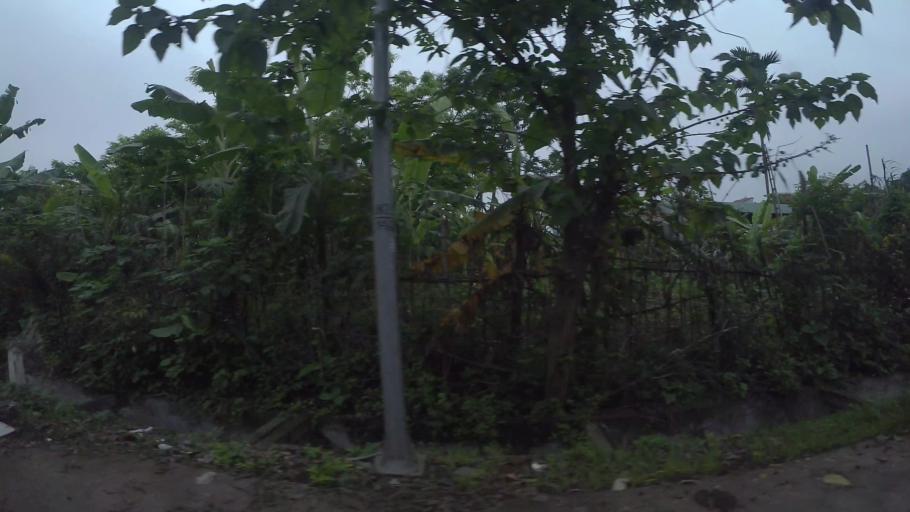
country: VN
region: Hung Yen
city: Van Giang
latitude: 20.9744
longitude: 105.8915
